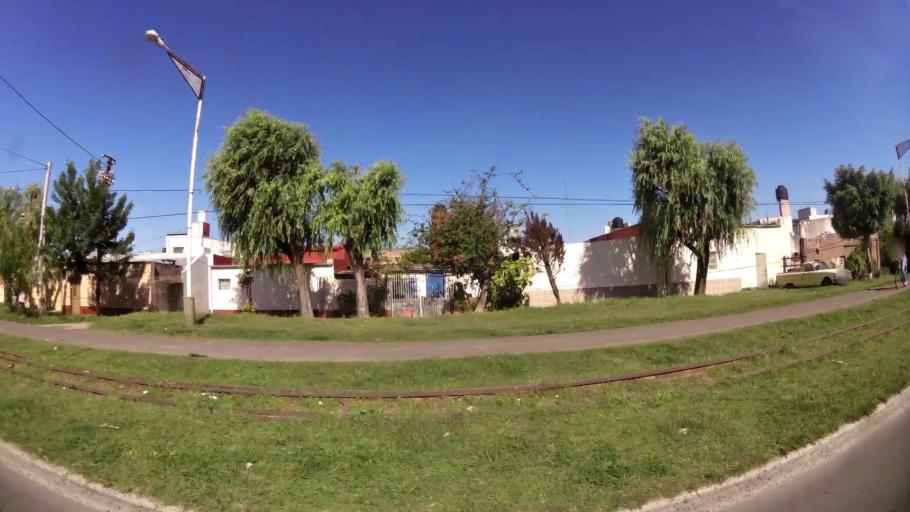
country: AR
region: Santa Fe
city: Santa Fe de la Vera Cruz
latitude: -31.6265
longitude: -60.6979
